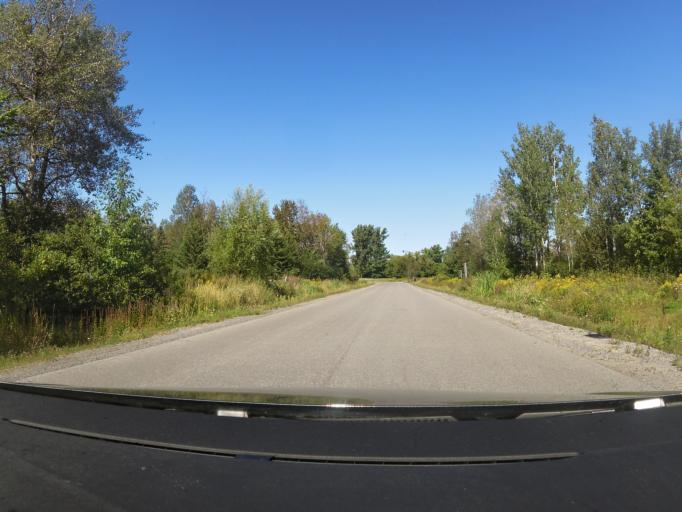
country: CA
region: Ontario
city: Bells Corners
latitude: 45.2739
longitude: -76.0021
